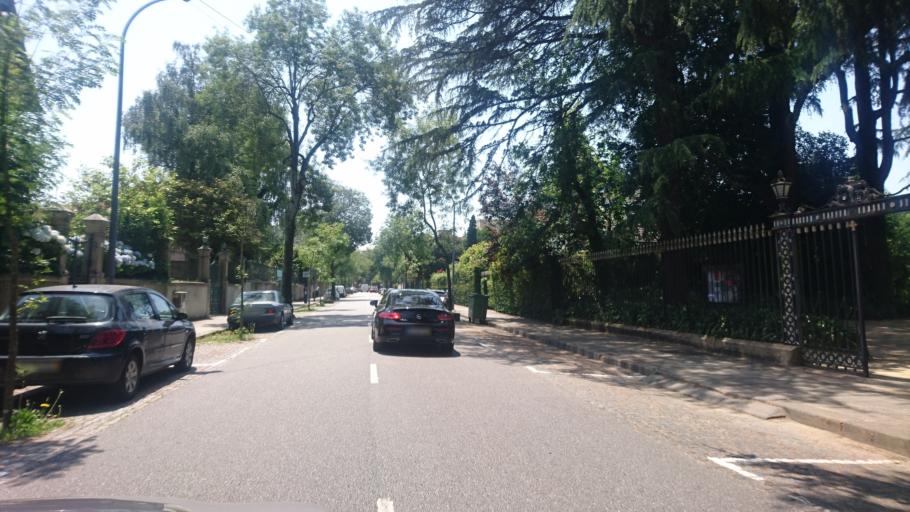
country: PT
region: Porto
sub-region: Porto
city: Porto
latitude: 41.1559
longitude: -8.6419
